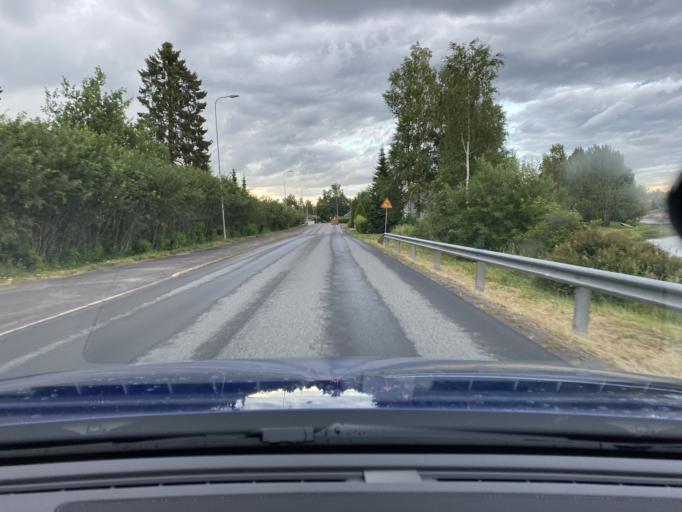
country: FI
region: Satakunta
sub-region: Pori
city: Huittinen
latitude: 61.1714
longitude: 22.6874
